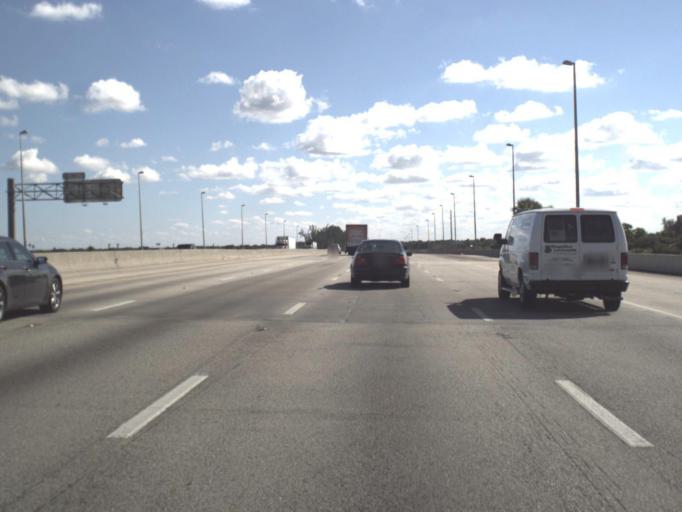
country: US
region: Florida
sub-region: Palm Beach County
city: Villages of Oriole
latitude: 26.4542
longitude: -80.1747
